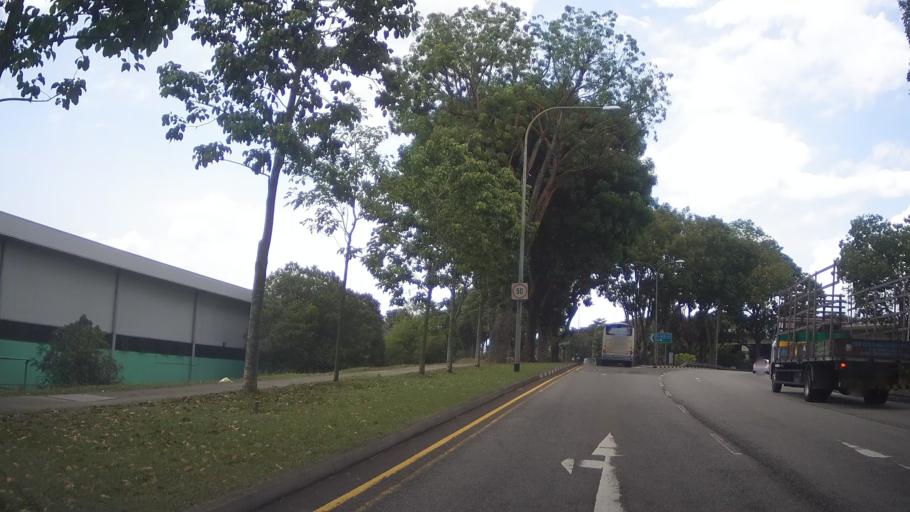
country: MY
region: Johor
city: Johor Bahru
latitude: 1.3303
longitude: 103.6764
